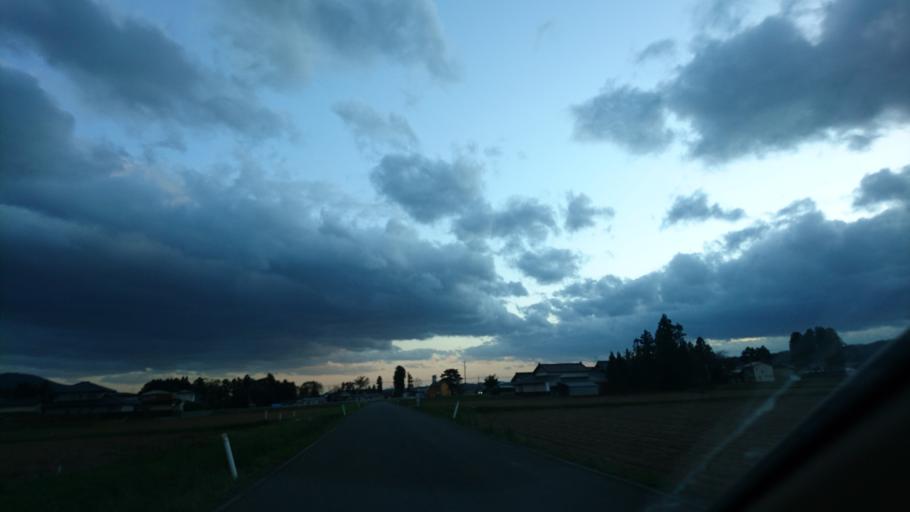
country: JP
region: Iwate
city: Mizusawa
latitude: 39.0667
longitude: 141.1411
